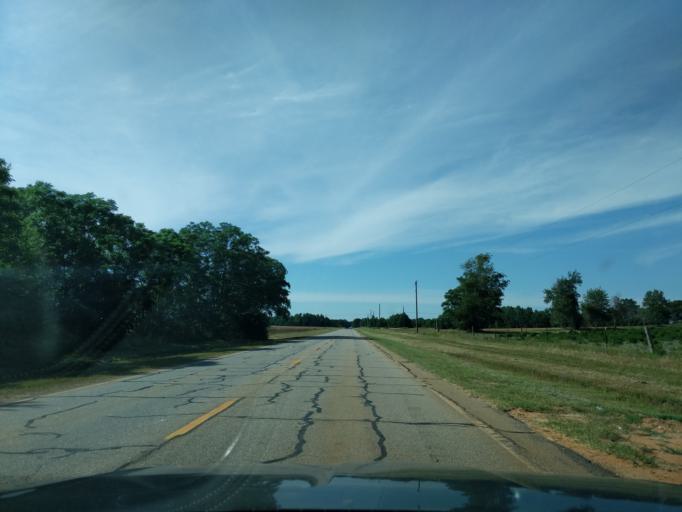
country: US
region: Georgia
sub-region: Jefferson County
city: Wrens
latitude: 33.2285
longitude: -82.3808
